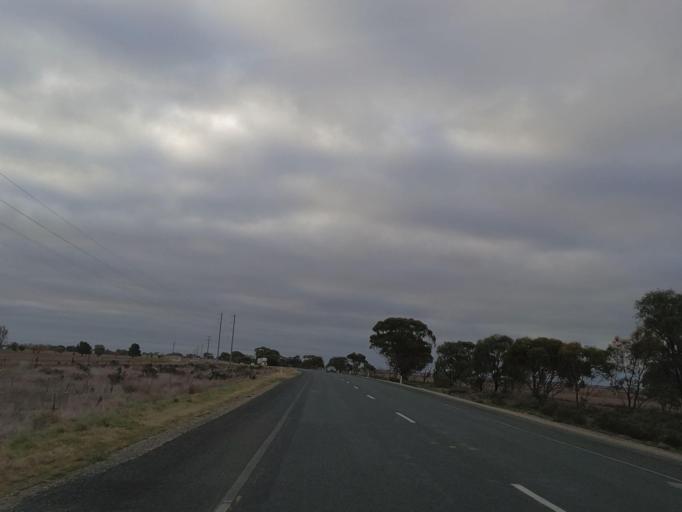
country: AU
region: Victoria
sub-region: Swan Hill
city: Swan Hill
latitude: -35.5856
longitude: 143.7903
